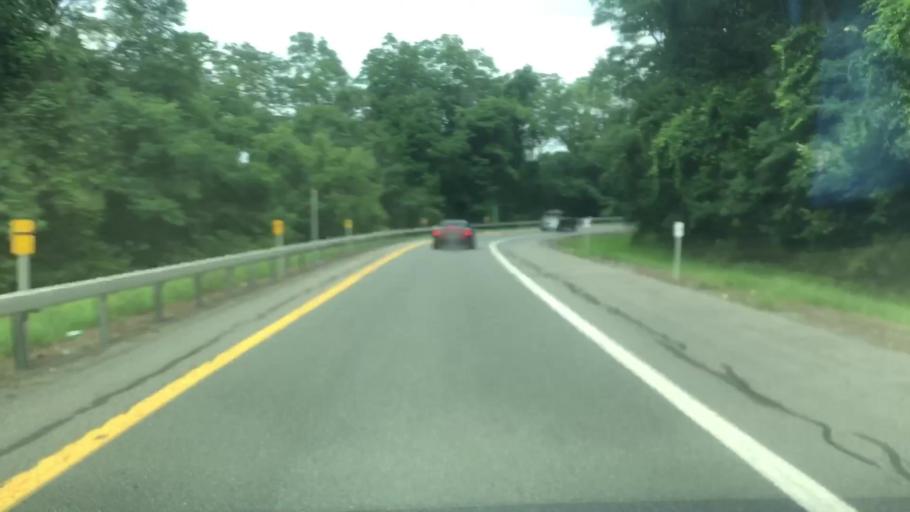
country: US
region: New York
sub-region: Schenectady County
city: Schenectady
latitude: 42.7827
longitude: -73.9252
